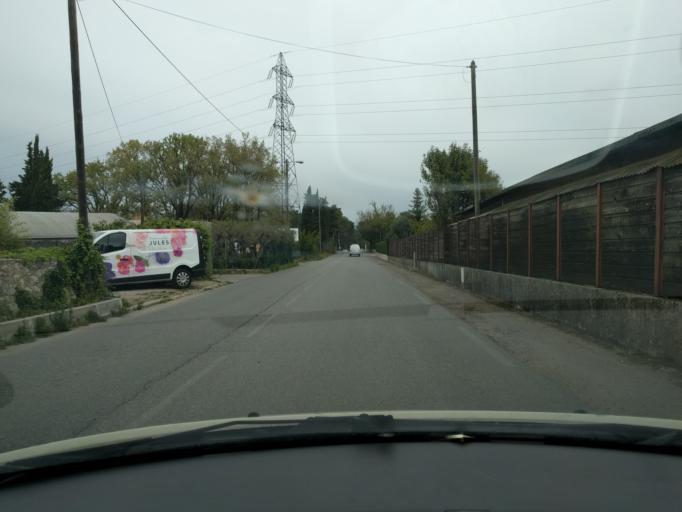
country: FR
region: Provence-Alpes-Cote d'Azur
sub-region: Departement des Alpes-Maritimes
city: La Roquette-sur-Siagne
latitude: 43.6004
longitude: 6.9580
